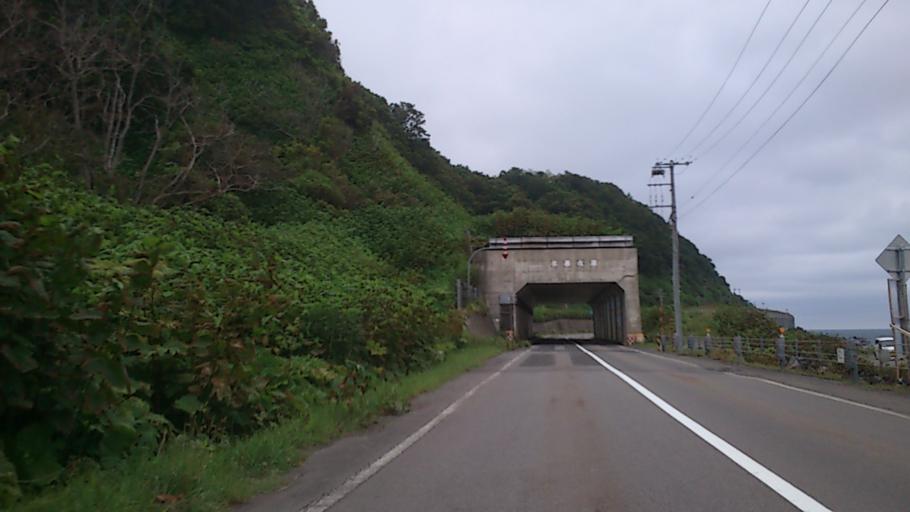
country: JP
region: Hokkaido
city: Iwanai
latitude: 42.6879
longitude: 139.9369
